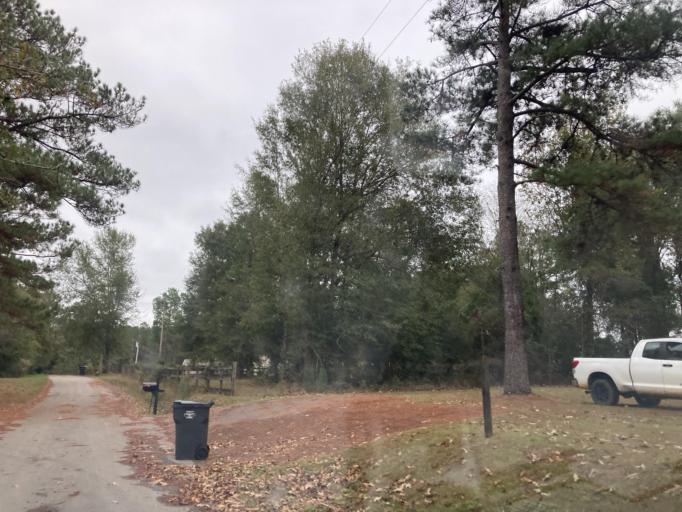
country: US
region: Mississippi
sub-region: Lamar County
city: Purvis
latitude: 31.1848
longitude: -89.4123
